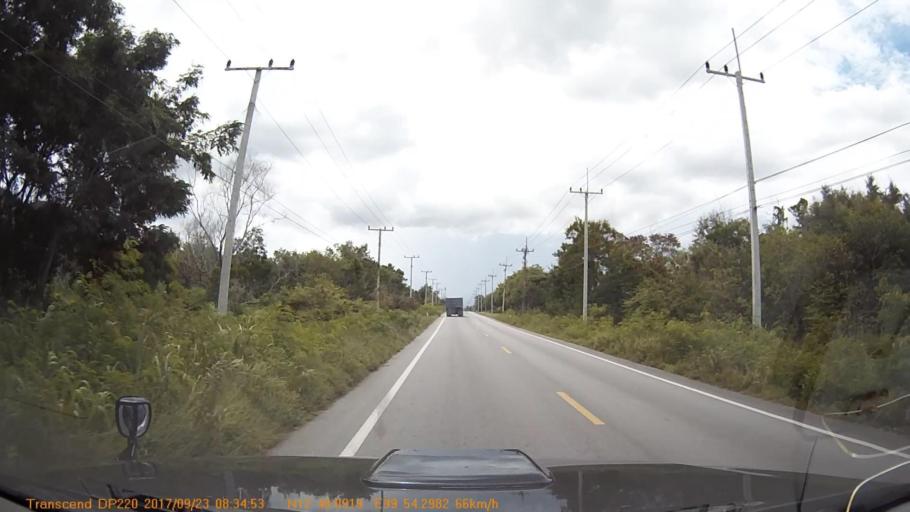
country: TH
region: Prachuap Khiri Khan
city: Hua Hin
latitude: 12.6682
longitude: 99.9049
